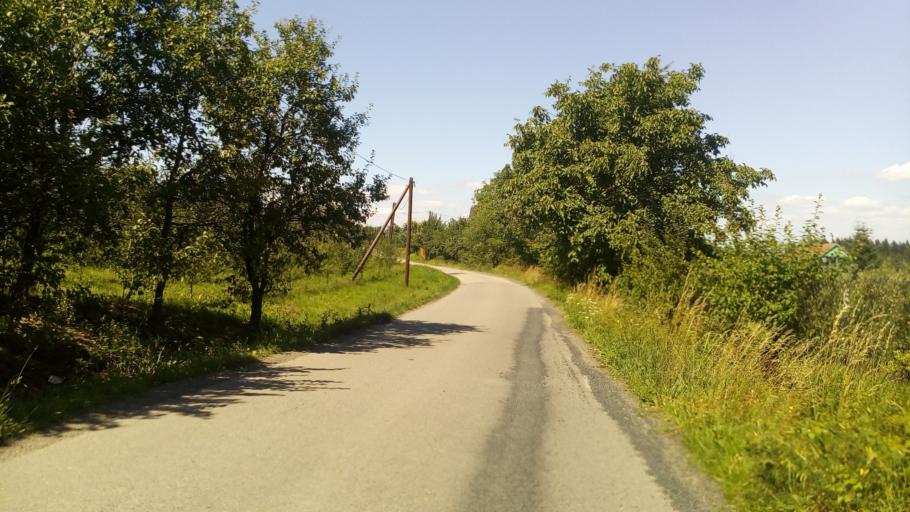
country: PL
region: Lesser Poland Voivodeship
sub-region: Powiat nowosadecki
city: Olszana
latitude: 49.5634
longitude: 20.4990
